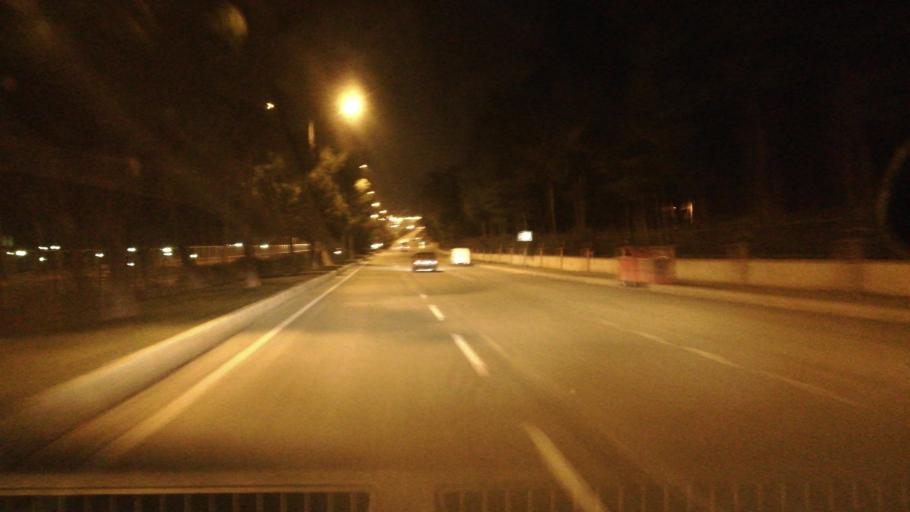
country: TR
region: Kahramanmaras
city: Kahramanmaras
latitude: 37.5992
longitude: 36.9226
